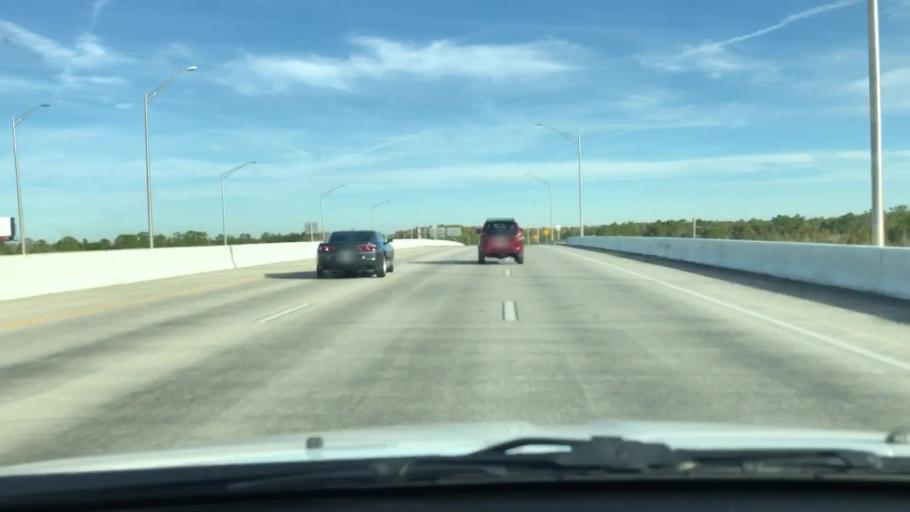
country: US
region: Florida
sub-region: Orange County
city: Meadow Woods
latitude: 28.3825
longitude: -81.3086
